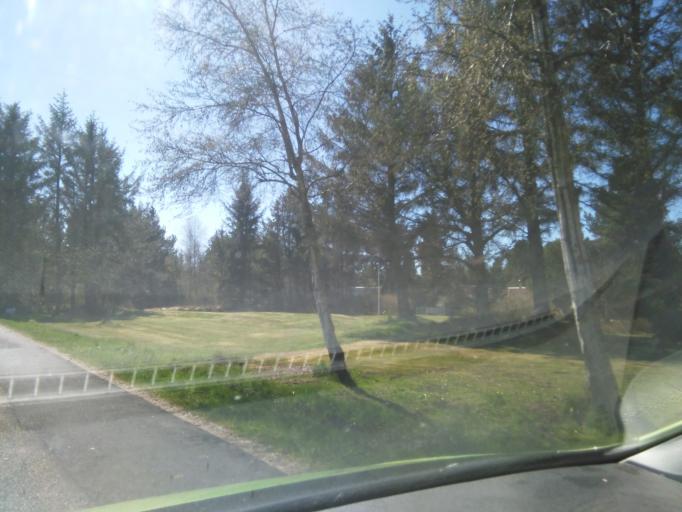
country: DK
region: South Denmark
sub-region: Varde Kommune
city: Oksbol
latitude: 55.5614
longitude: 8.2257
